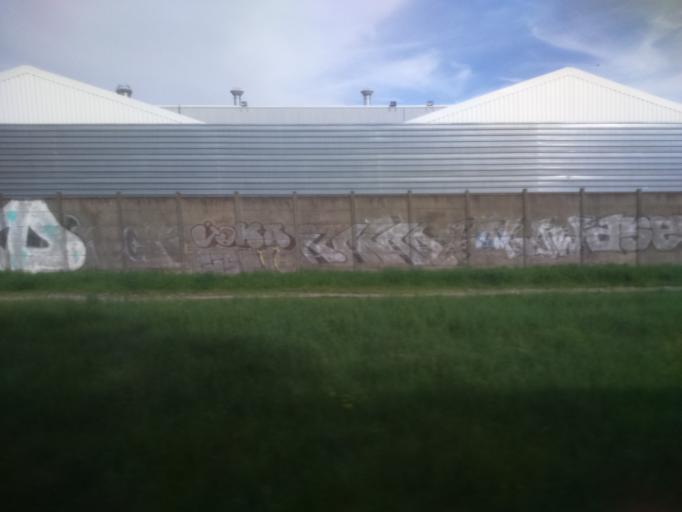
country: FR
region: Rhone-Alpes
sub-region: Departement de l'Isere
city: Grenoble
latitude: 45.1495
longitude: 5.7071
